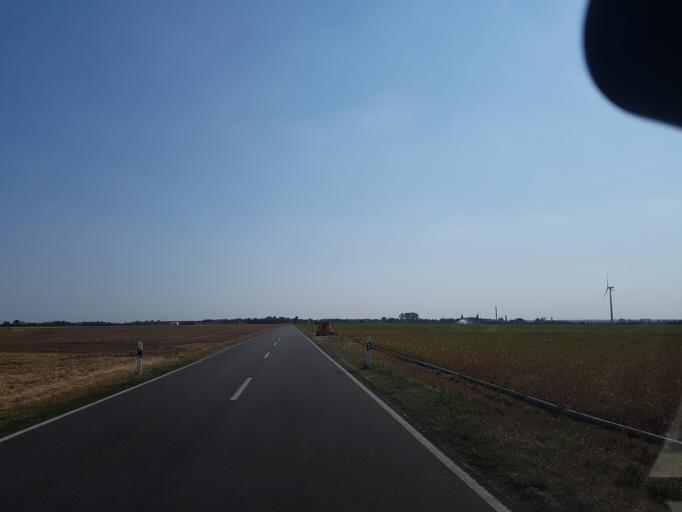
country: DE
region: Saxony-Anhalt
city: Prettin
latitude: 51.6606
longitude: 12.9895
